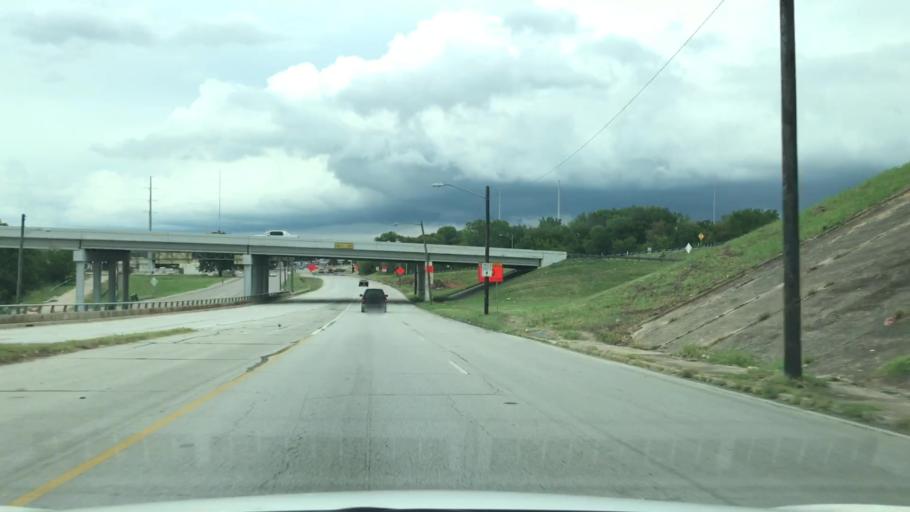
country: US
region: Texas
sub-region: Tarrant County
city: Fort Worth
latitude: 32.7461
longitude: -97.3074
